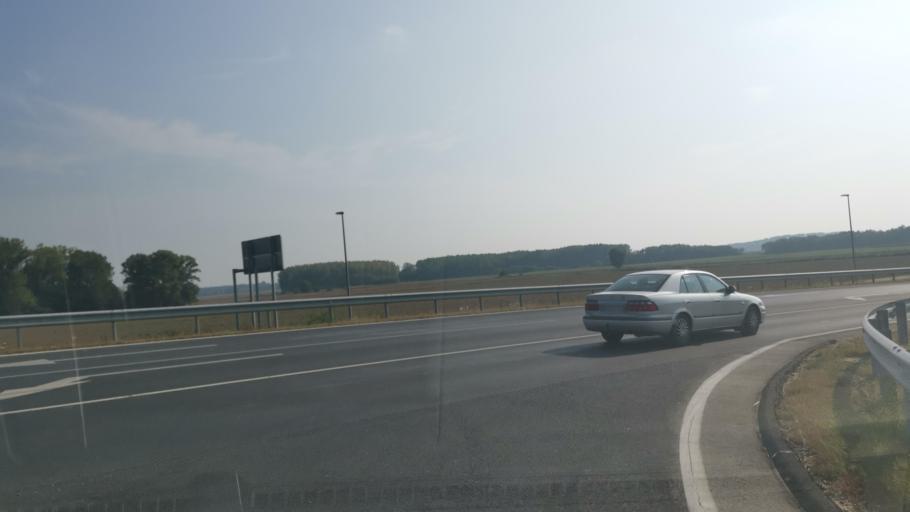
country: HU
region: Vas
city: Repcelak
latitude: 47.4091
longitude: 17.0190
